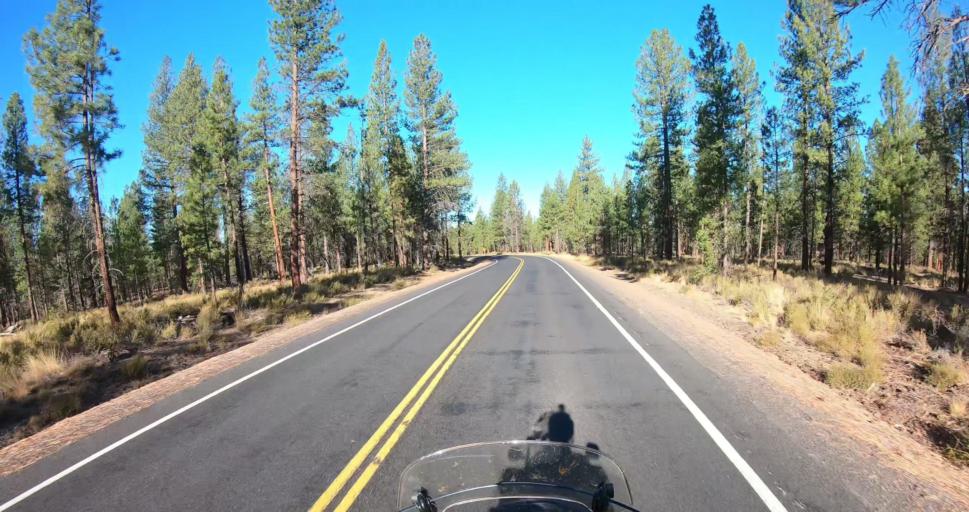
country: US
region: Oregon
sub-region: Deschutes County
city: La Pine
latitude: 43.7350
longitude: -121.4432
